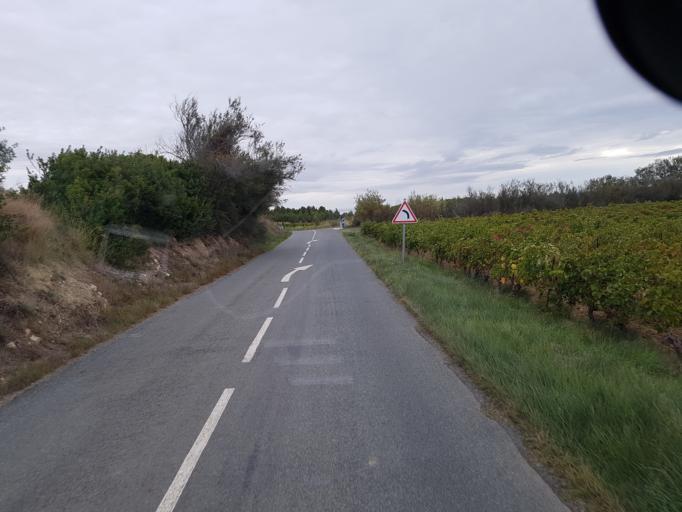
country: FR
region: Languedoc-Roussillon
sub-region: Departement de l'Aude
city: Narbonne
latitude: 43.1426
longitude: 2.9823
